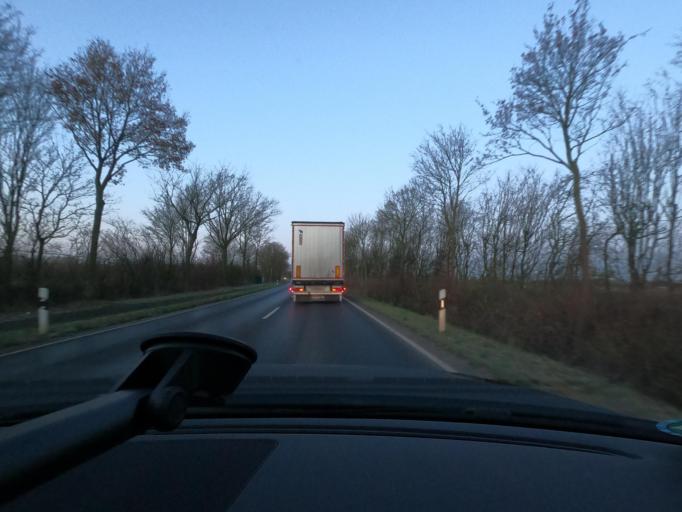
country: DE
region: North Rhine-Westphalia
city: Kempen
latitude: 51.3355
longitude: 6.4120
